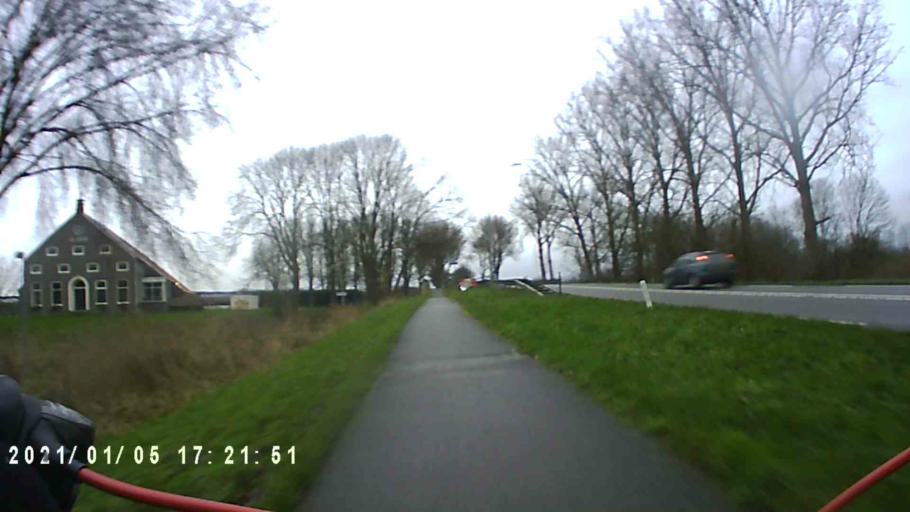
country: NL
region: Groningen
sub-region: Gemeente Delfzijl
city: Delfzijl
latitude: 53.2361
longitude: 6.9643
